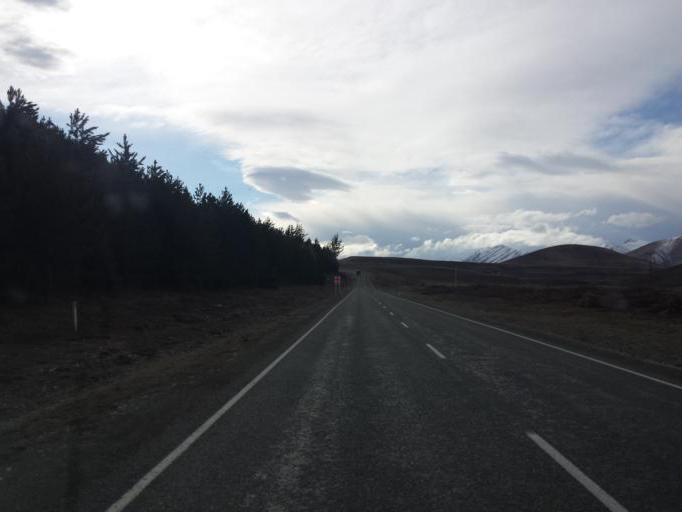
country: NZ
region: Canterbury
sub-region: Timaru District
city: Pleasant Point
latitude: -44.0467
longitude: 170.5060
